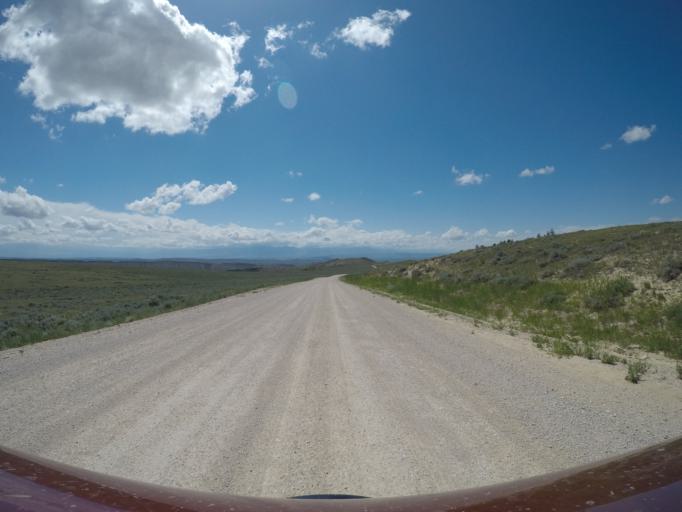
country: US
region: Wyoming
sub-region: Park County
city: Powell
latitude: 45.2065
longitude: -108.7776
